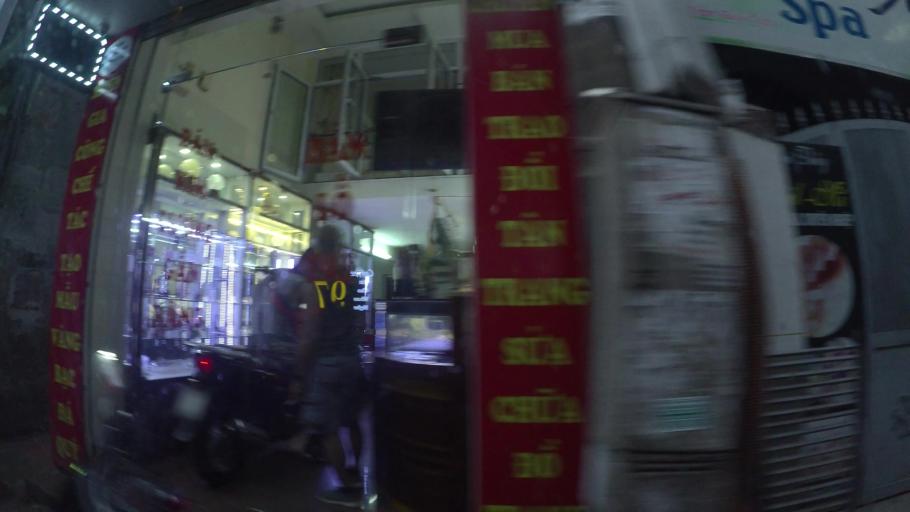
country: VN
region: Ha Noi
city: Hanoi
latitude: 21.0217
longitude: 105.8392
